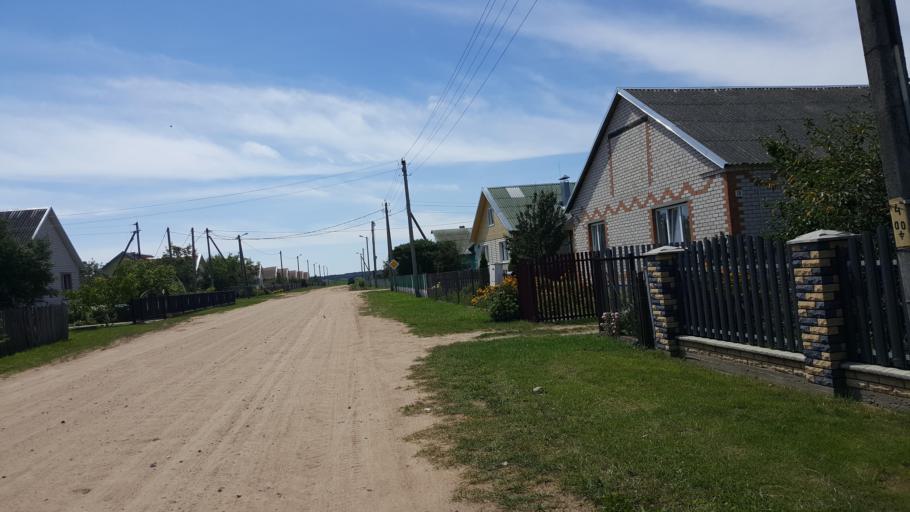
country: BY
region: Brest
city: Pruzhany
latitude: 52.5528
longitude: 24.2052
